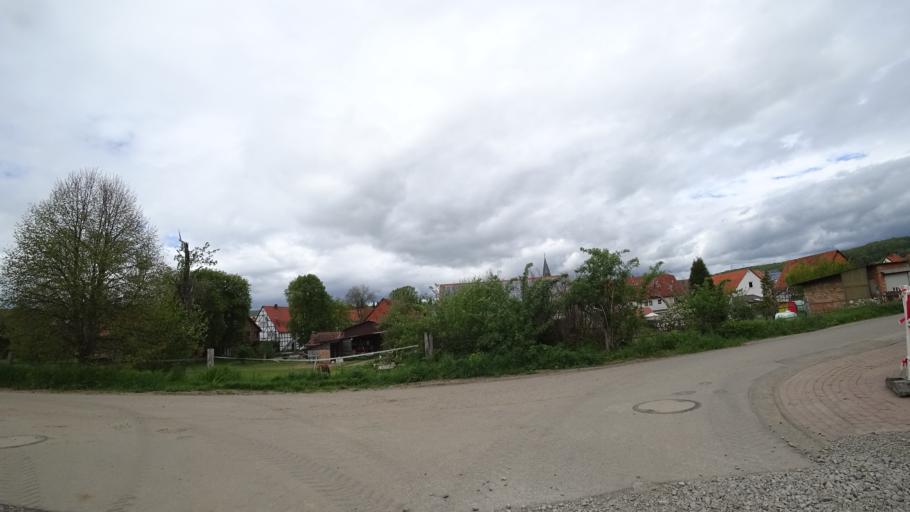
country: DE
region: Hesse
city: Liebenau
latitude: 51.4573
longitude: 9.3066
